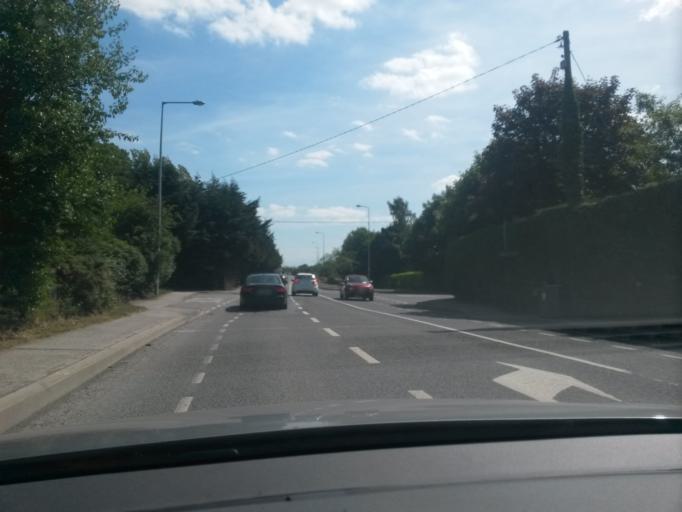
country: IE
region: Leinster
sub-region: Kildare
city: Sallins
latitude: 53.2429
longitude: -6.6657
